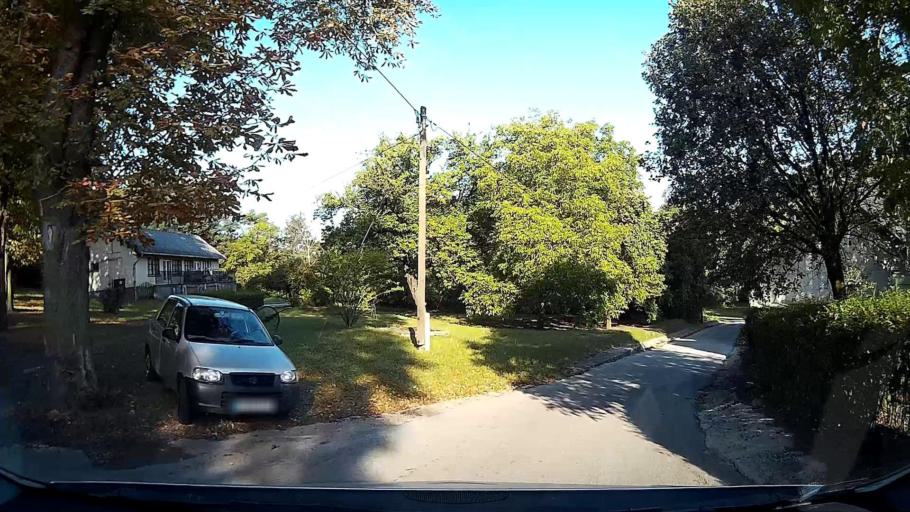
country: HU
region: Pest
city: Nagymaros
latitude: 47.7592
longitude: 18.9396
